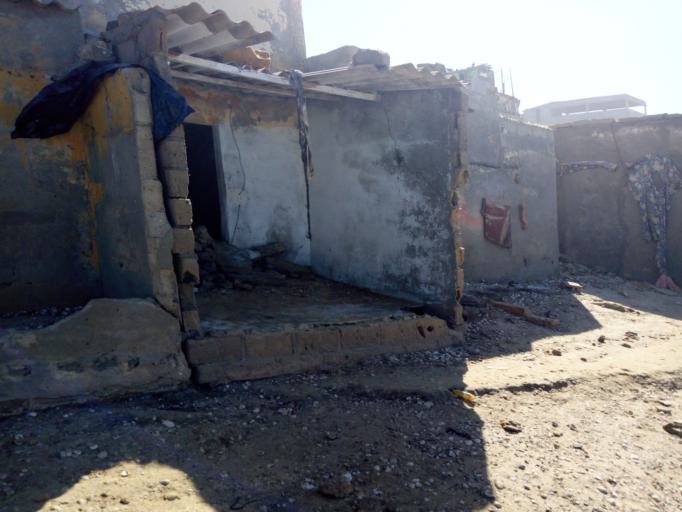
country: SN
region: Saint-Louis
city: Saint-Louis
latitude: 16.0272
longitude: -16.5092
